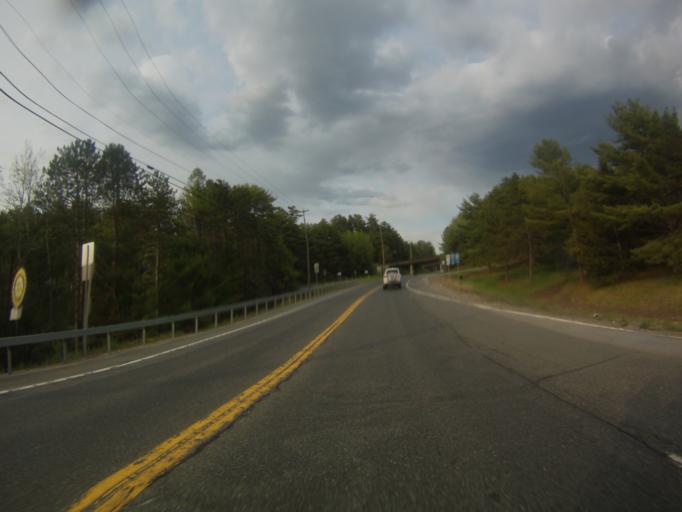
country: US
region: New York
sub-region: Warren County
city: Warrensburg
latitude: 43.6676
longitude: -73.7813
